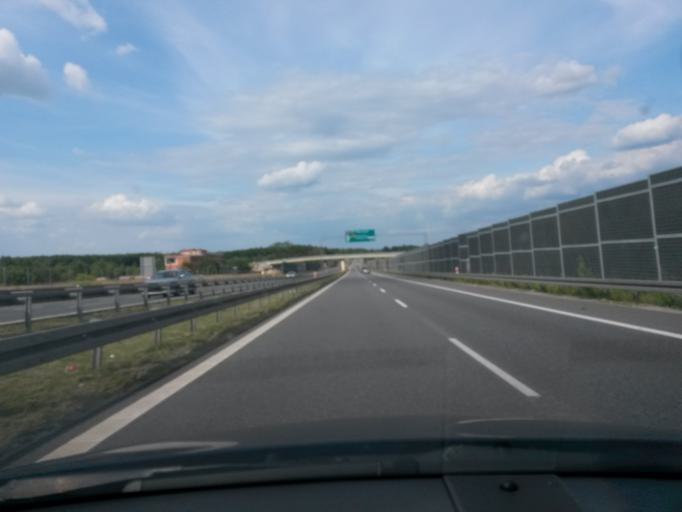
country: PL
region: Masovian Voivodeship
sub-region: Powiat zyrardowski
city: Radziejowice
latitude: 51.9945
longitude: 20.5481
